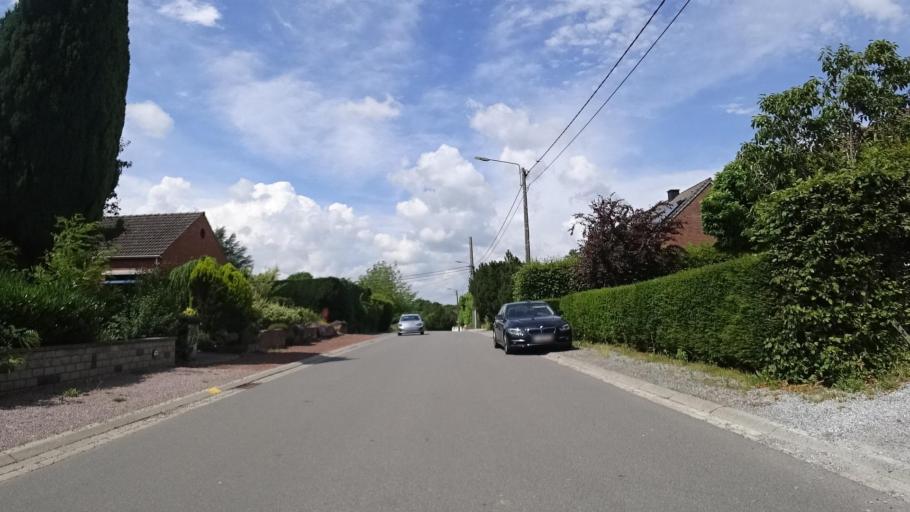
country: BE
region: Wallonia
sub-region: Province du Brabant Wallon
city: Perwez
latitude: 50.5887
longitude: 4.7789
